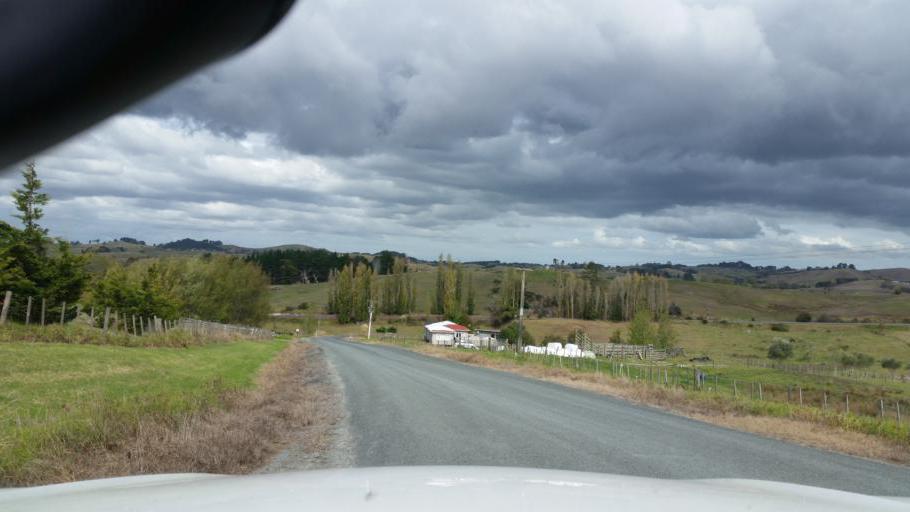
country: NZ
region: Northland
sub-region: Whangarei
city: Ruakaka
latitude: -36.1078
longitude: 174.2771
